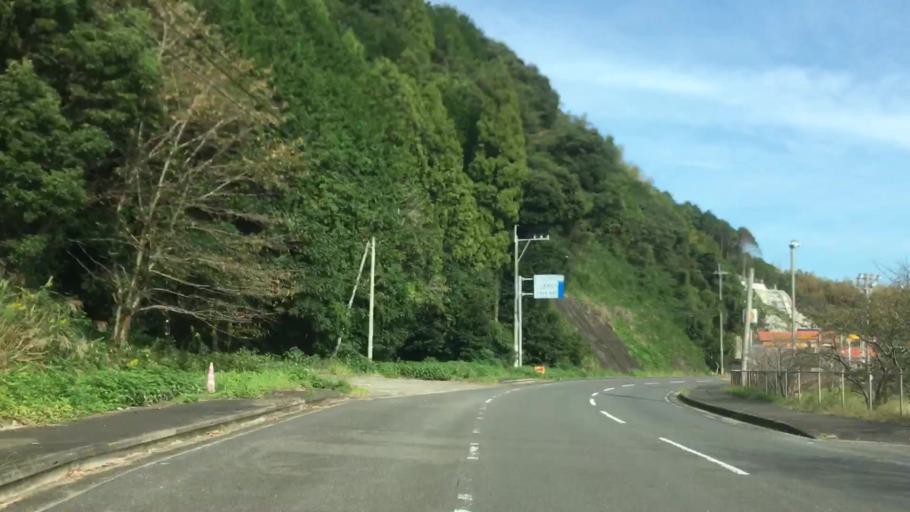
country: JP
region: Nagasaki
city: Sasebo
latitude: 32.9921
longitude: 129.6513
